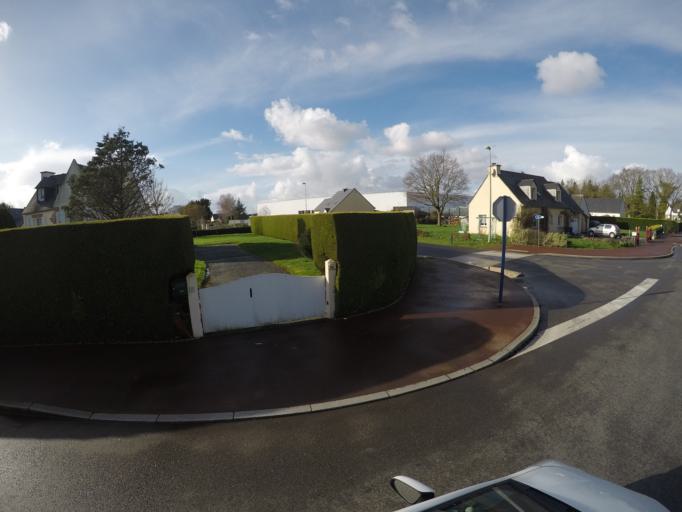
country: FR
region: Brittany
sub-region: Departement des Cotes-d'Armor
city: Lanvollon
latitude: 48.6363
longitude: -2.9870
